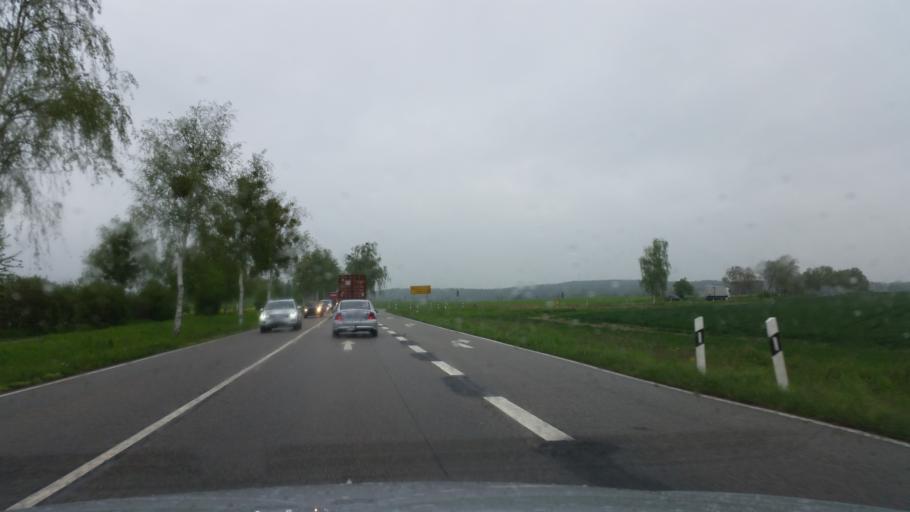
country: DE
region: Saxony-Anhalt
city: Kalbe
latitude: 52.5893
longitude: 11.3444
